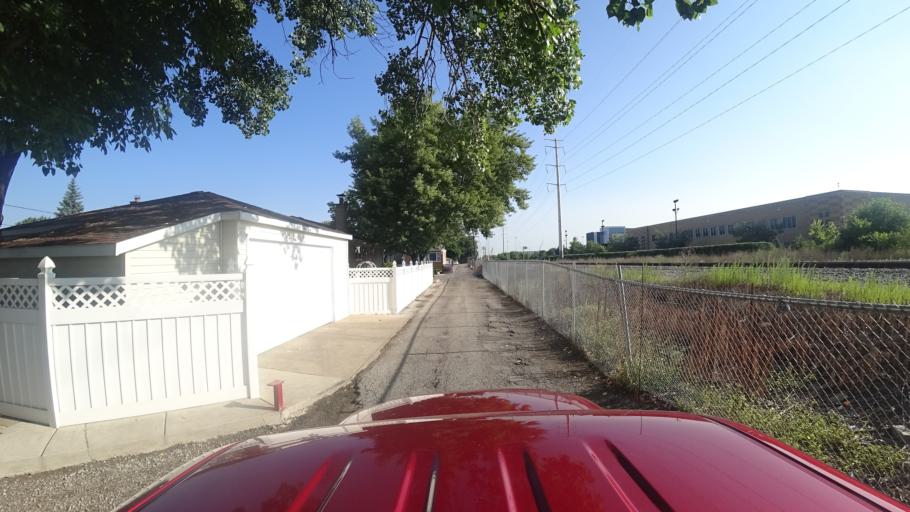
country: US
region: Illinois
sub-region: Cook County
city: Hometown
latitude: 41.7920
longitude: -87.7135
